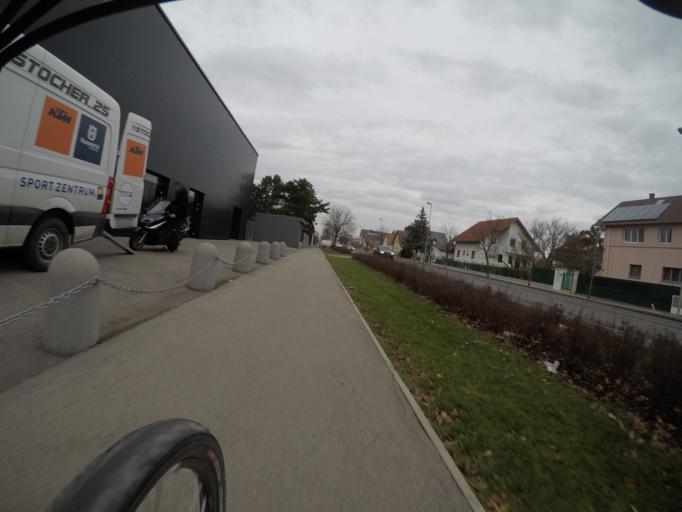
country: AT
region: Lower Austria
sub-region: Politischer Bezirk Modling
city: Vosendorf
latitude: 48.1327
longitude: 16.3261
